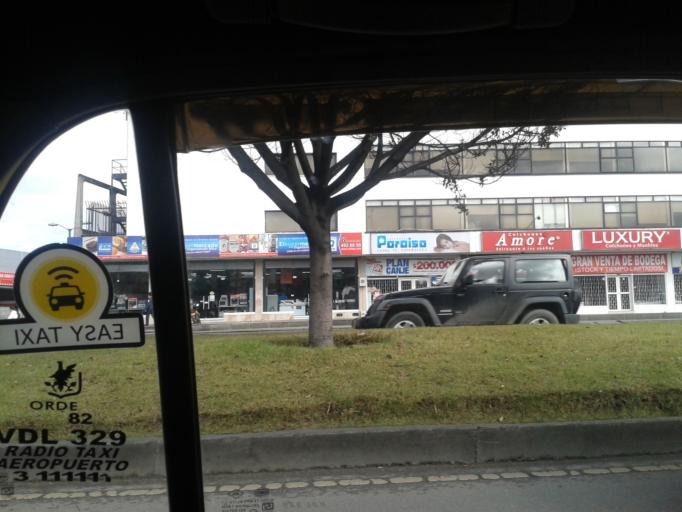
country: CO
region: Bogota D.C.
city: Bogota
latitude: 4.6301
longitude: -74.1219
